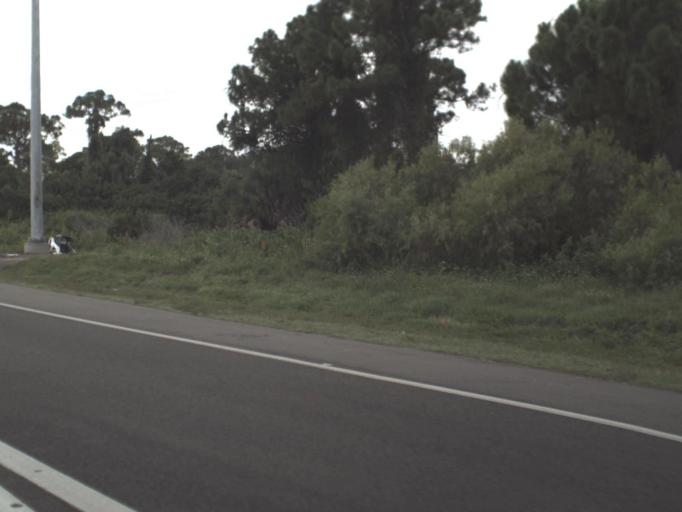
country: US
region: Florida
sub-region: Sarasota County
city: Nokomis
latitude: 27.1348
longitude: -82.4083
